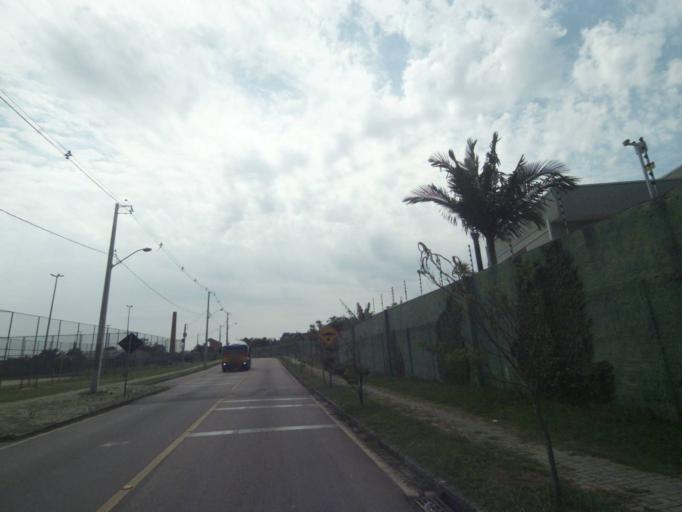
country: BR
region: Parana
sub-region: Curitiba
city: Curitiba
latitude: -25.4718
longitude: -49.3229
